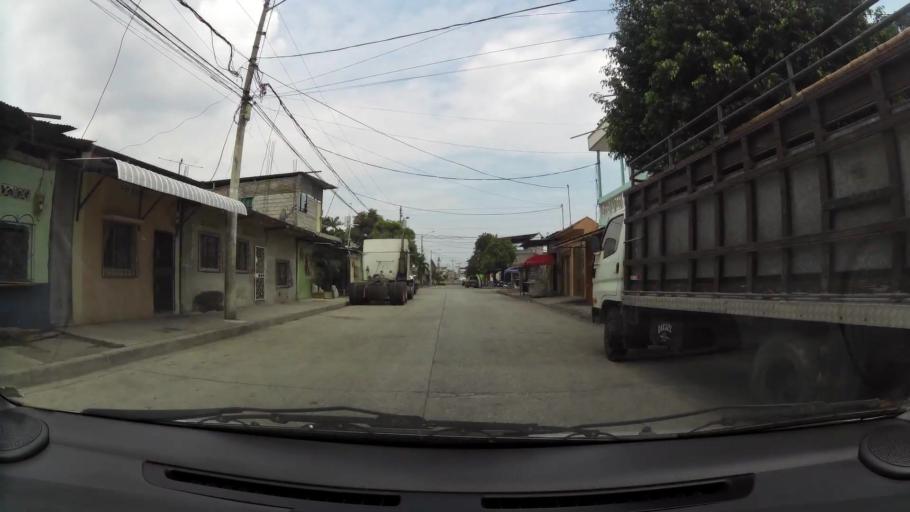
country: EC
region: Guayas
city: Guayaquil
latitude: -2.2384
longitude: -79.9192
